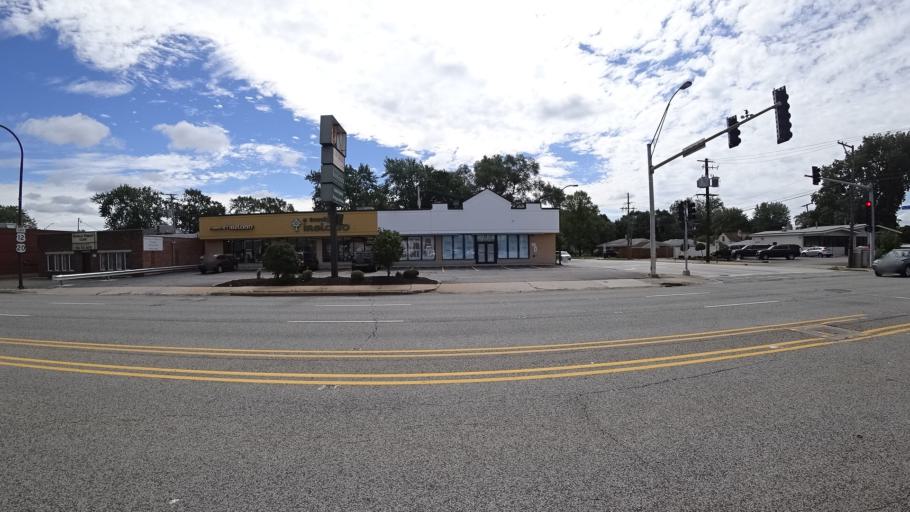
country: US
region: Illinois
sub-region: Cook County
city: Burbank
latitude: 41.7195
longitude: -87.7894
